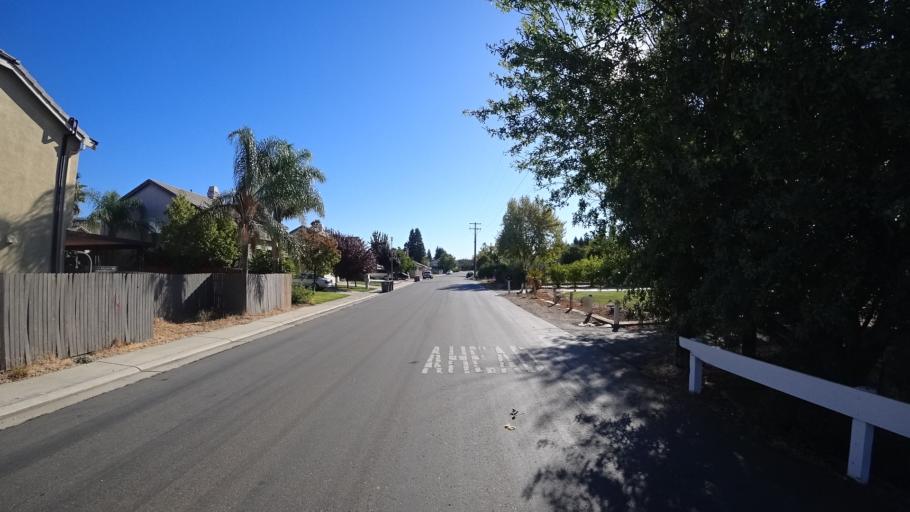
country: US
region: California
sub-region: Sacramento County
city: Vineyard
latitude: 38.4490
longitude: -121.3636
